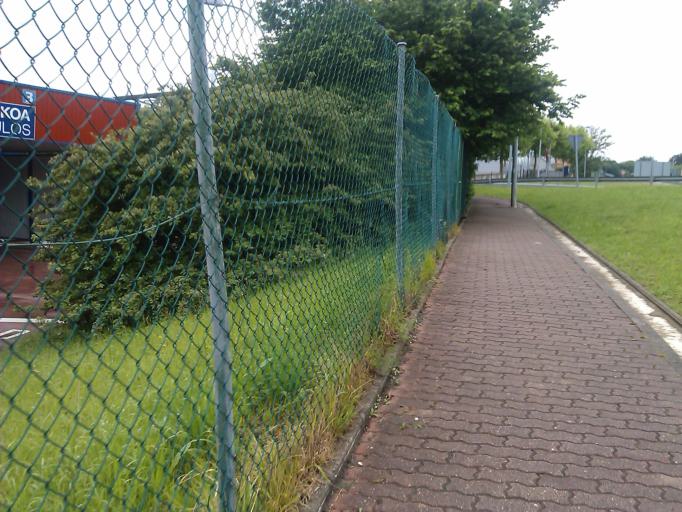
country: ES
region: Basque Country
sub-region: Provincia de Guipuzcoa
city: Urnieta
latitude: 43.2407
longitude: -1.9955
